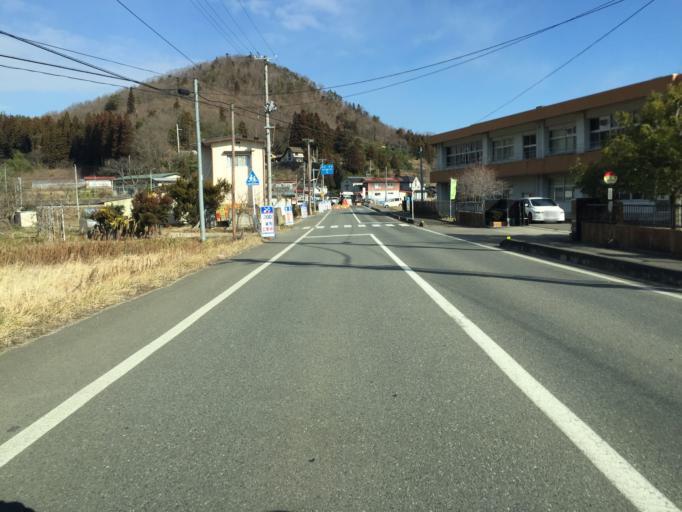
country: JP
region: Fukushima
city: Hobaramachi
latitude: 37.7668
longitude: 140.5787
